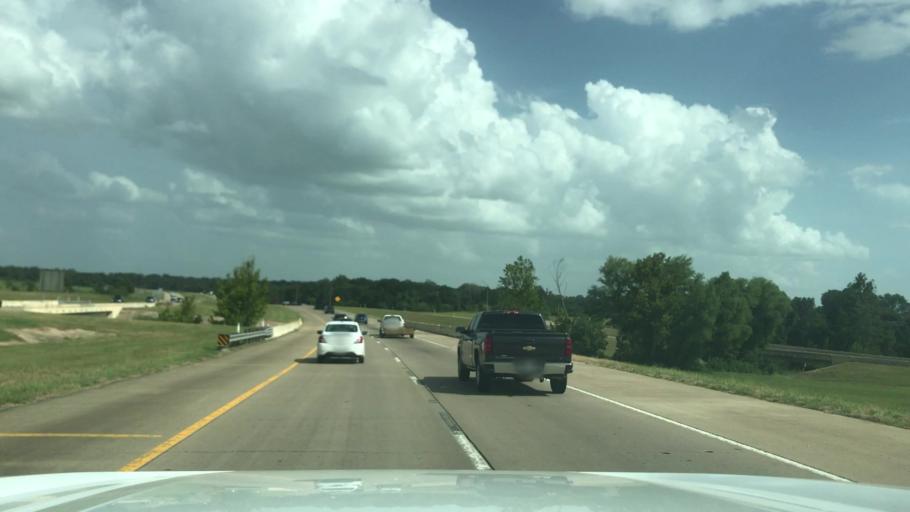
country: US
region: Texas
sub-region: Waller County
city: Hempstead
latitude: 30.0979
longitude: -96.0407
